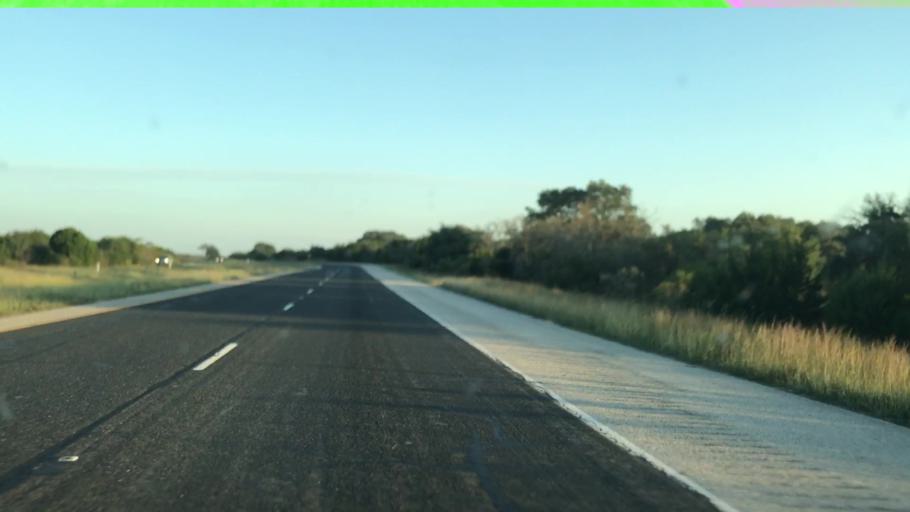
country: US
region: Texas
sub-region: Kerr County
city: Kerrville
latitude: 30.0618
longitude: -99.0500
